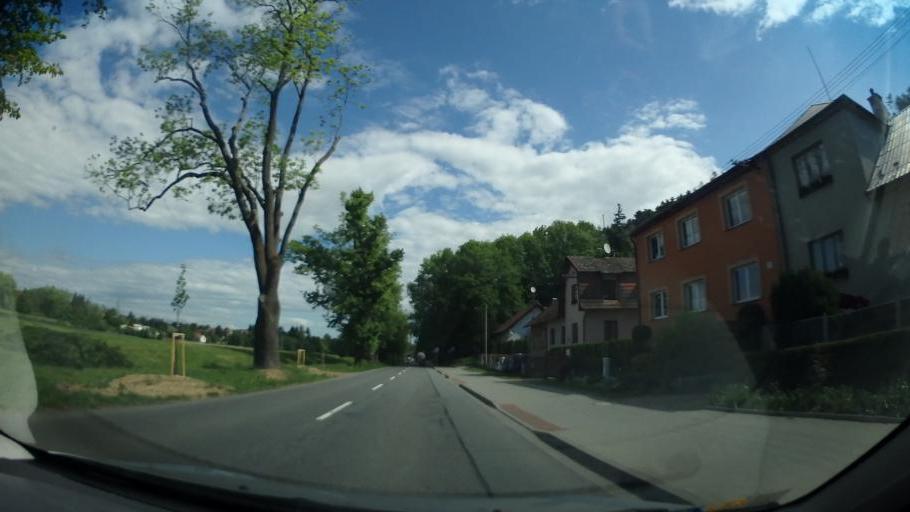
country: CZ
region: Pardubicky
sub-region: Okres Svitavy
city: Moravska Trebova
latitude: 49.7462
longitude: 16.6561
